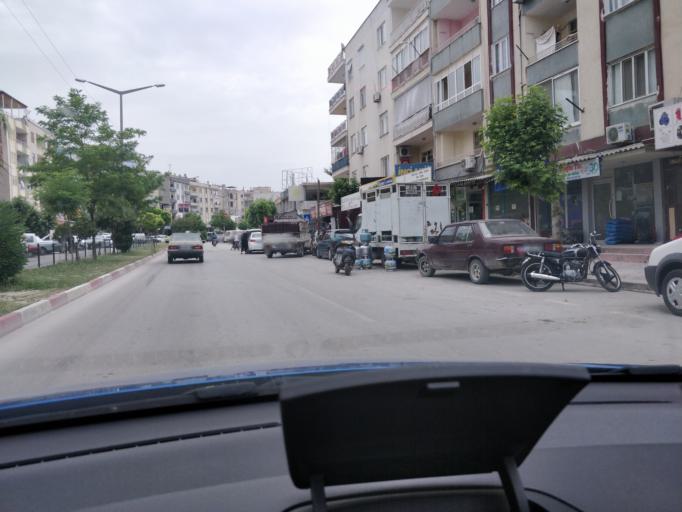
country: TR
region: Mersin
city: Mut
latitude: 36.6461
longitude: 33.4331
